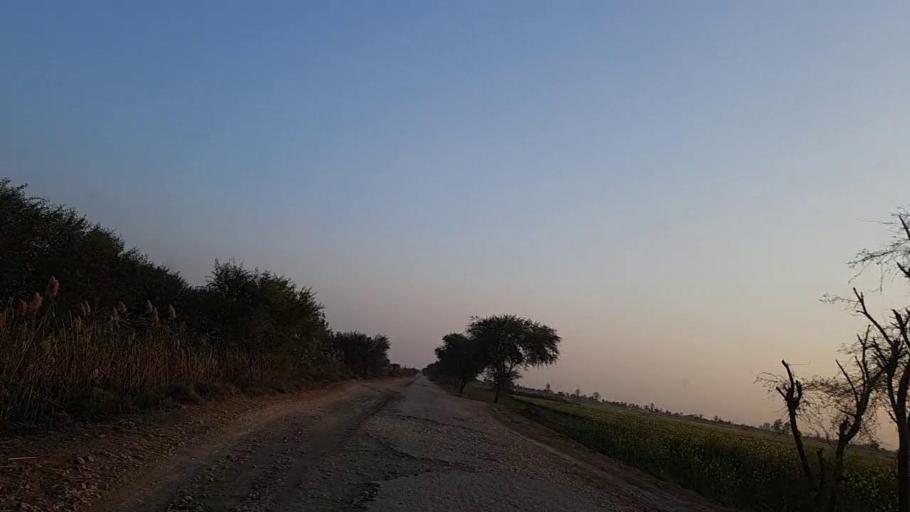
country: PK
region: Sindh
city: Shahdadpur
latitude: 25.9341
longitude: 68.5048
